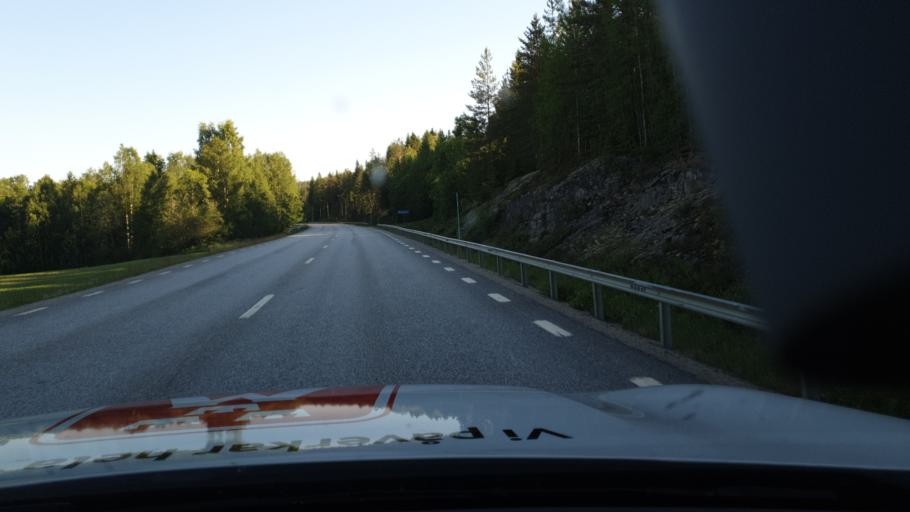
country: SE
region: Vaesterbotten
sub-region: Vannas Kommun
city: Vannasby
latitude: 64.1136
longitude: 19.9712
